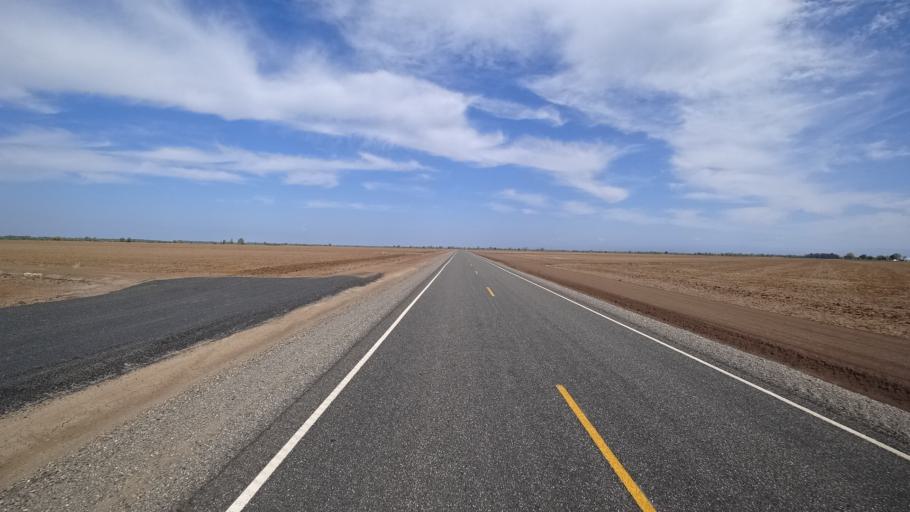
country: US
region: California
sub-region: Butte County
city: Durham
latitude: 39.5307
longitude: -121.9299
